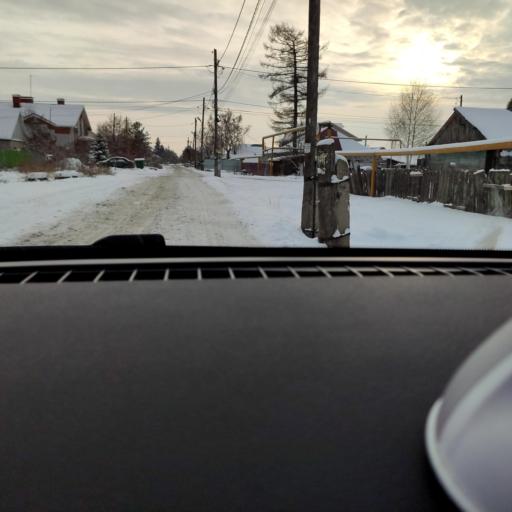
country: RU
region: Samara
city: Petra-Dubrava
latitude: 53.2539
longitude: 50.3436
